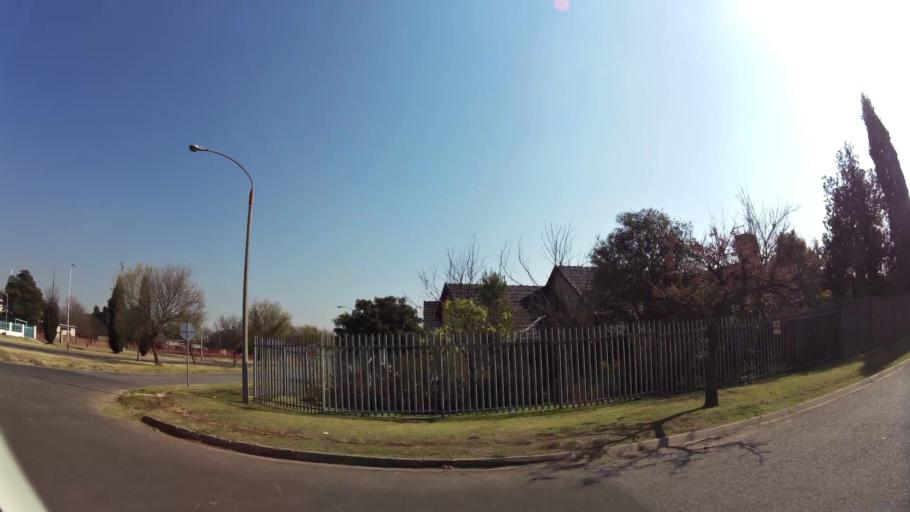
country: ZA
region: Gauteng
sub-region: Ekurhuleni Metropolitan Municipality
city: Boksburg
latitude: -26.2431
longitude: 28.2676
